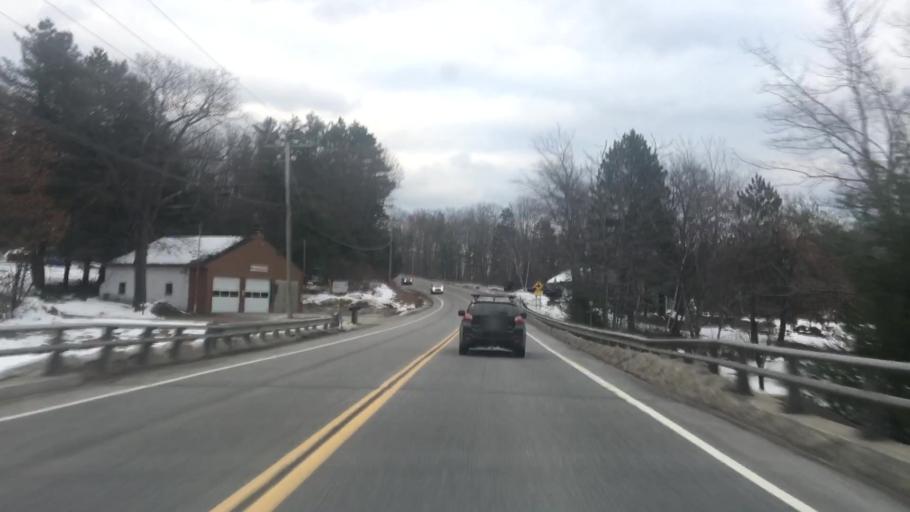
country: US
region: New Hampshire
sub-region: Hillsborough County
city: Antrim
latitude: 43.0814
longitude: -71.9705
